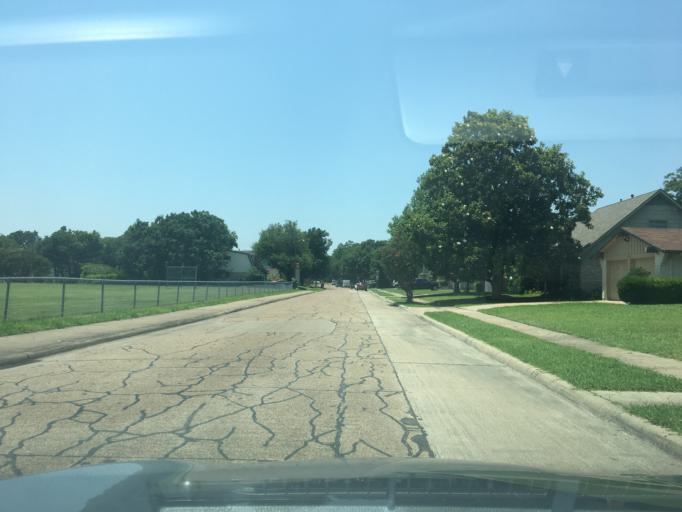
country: US
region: Texas
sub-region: Dallas County
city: Richardson
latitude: 32.9271
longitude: -96.6942
